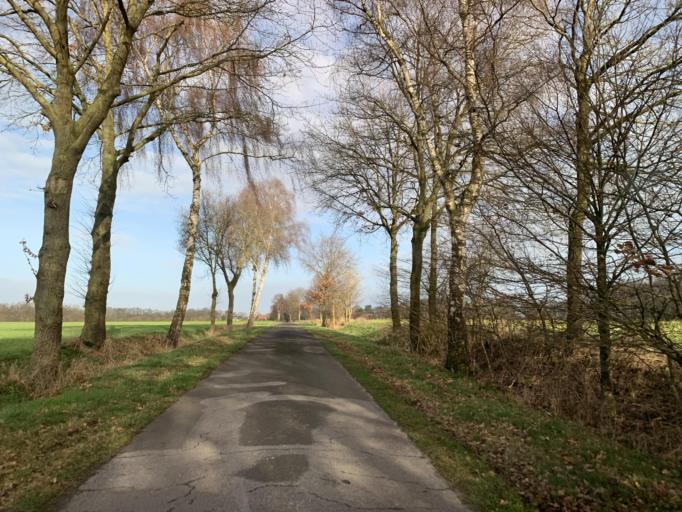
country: DE
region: North Rhine-Westphalia
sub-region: Regierungsbezirk Munster
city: Greven
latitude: 52.0488
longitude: 7.6455
